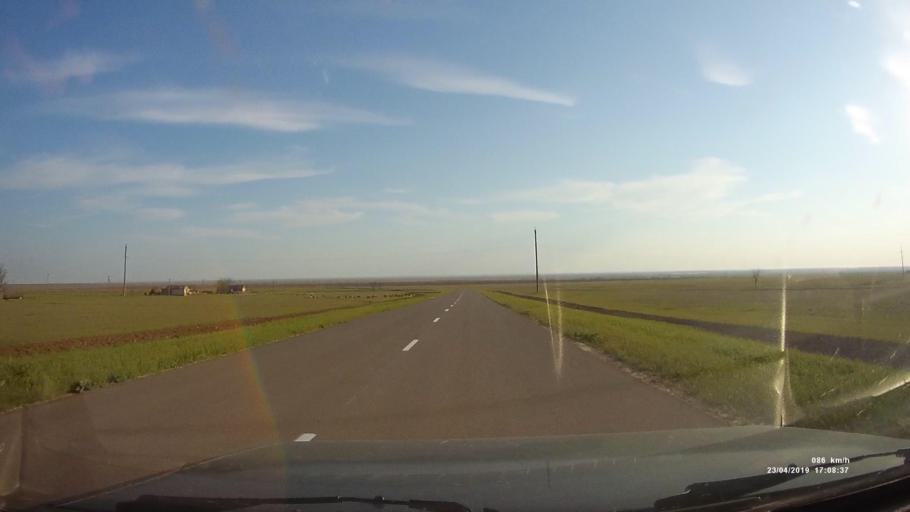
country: RU
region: Kalmykiya
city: Priyutnoye
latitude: 46.2691
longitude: 43.4863
